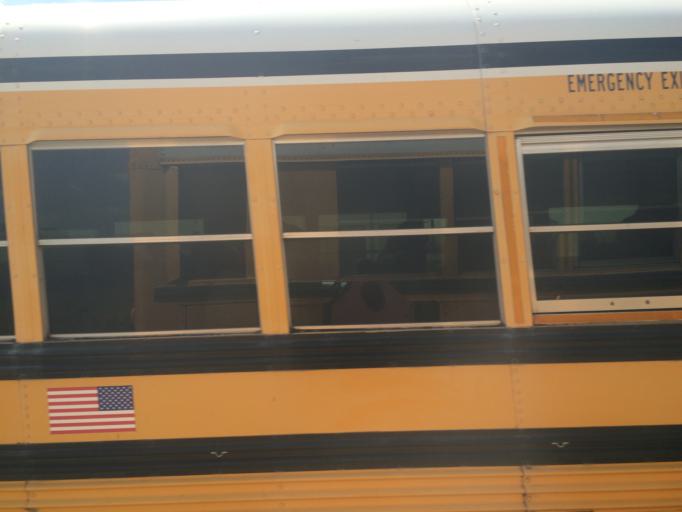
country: US
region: Florida
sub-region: Manatee County
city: Ellenton
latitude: 27.4708
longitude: -82.4323
